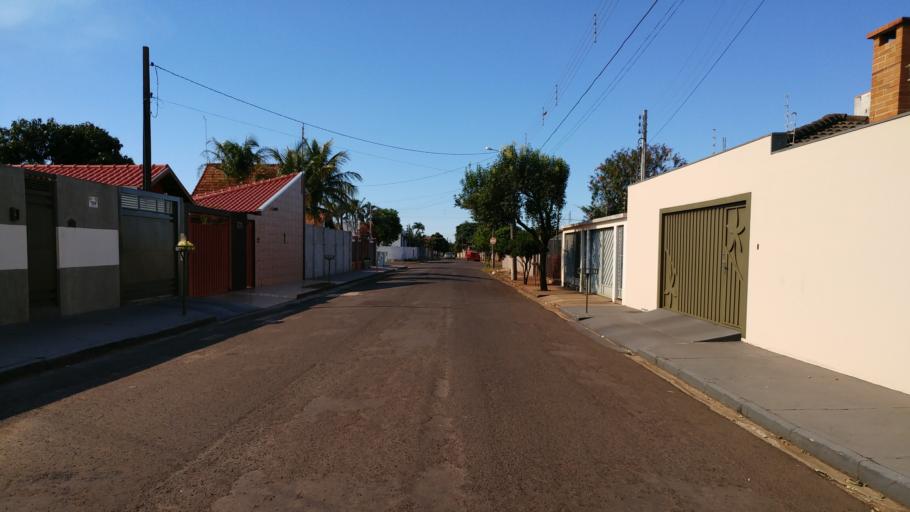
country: BR
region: Sao Paulo
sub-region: Paraguacu Paulista
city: Paraguacu Paulista
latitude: -22.4089
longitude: -50.5814
